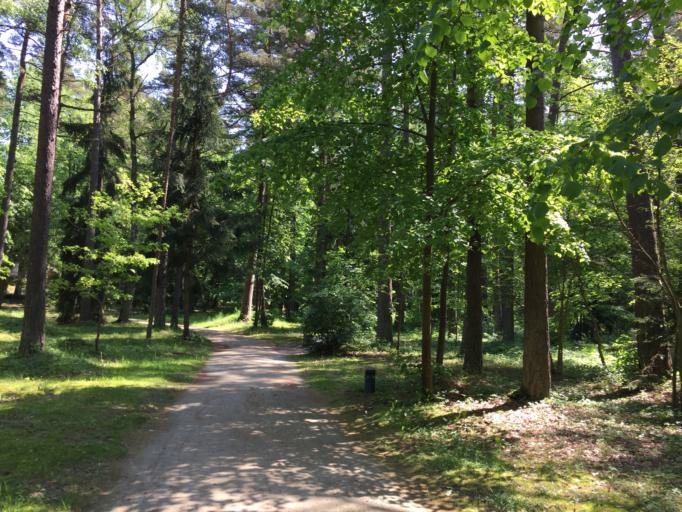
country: LT
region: Klaipedos apskritis
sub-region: Klaipeda
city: Palanga
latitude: 55.9045
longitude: 21.0575
